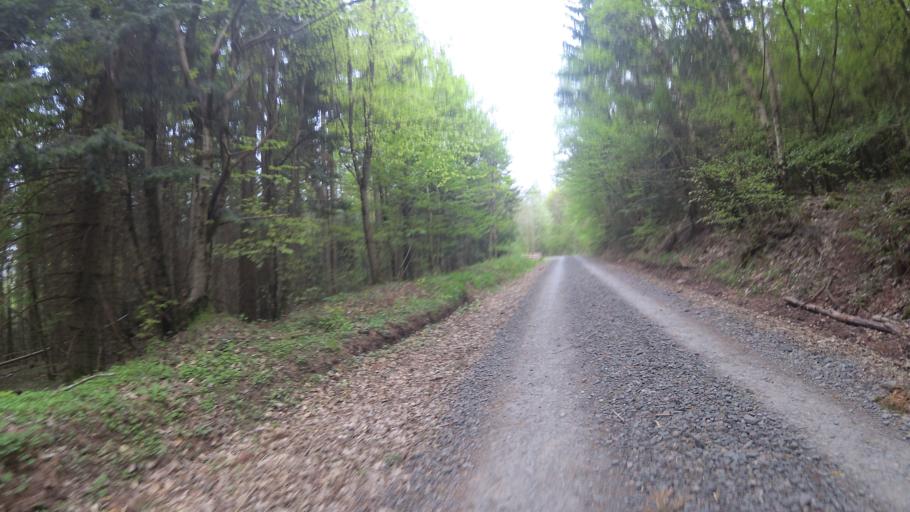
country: DE
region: Saarland
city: Mainzweiler
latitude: 49.4231
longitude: 7.1313
